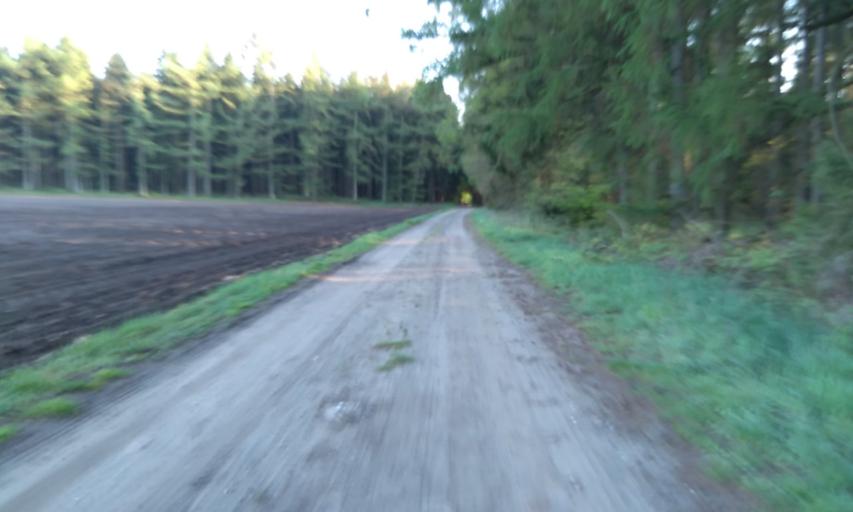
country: DE
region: Lower Saxony
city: Dollern
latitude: 53.5201
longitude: 9.5379
